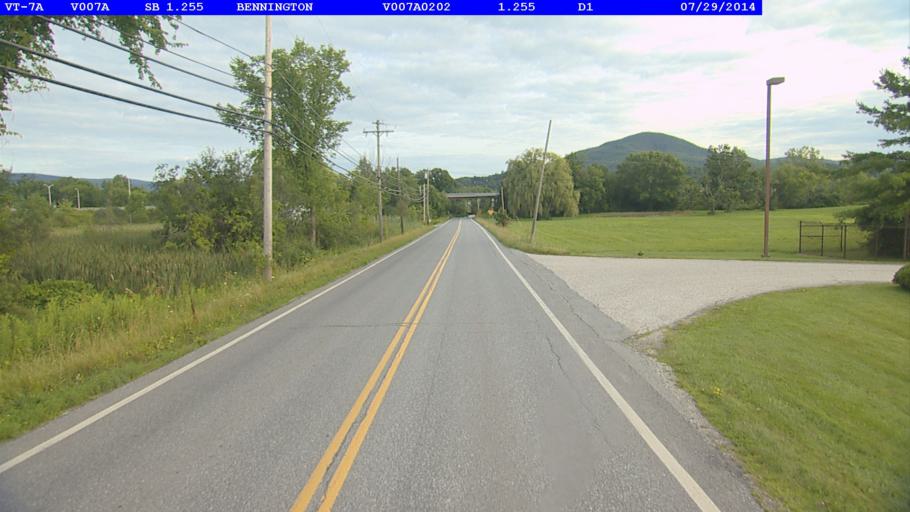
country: US
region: Vermont
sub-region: Bennington County
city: Bennington
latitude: 42.9077
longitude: -73.2116
